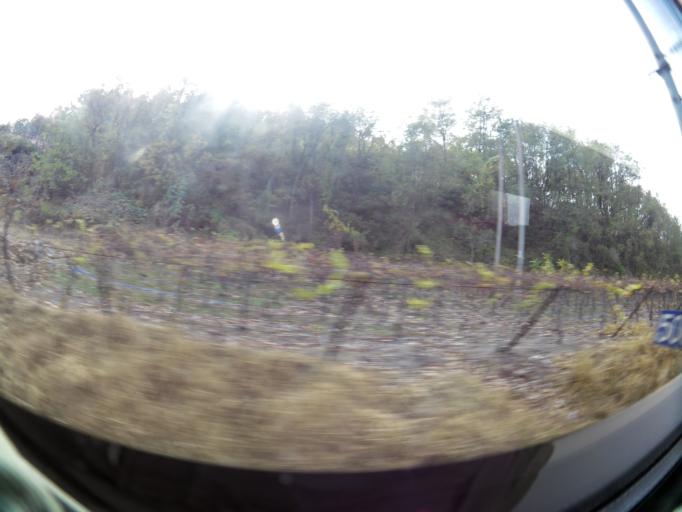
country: KR
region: Gyeongsangbuk-do
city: Gimcheon
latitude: 36.1278
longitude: 128.0311
